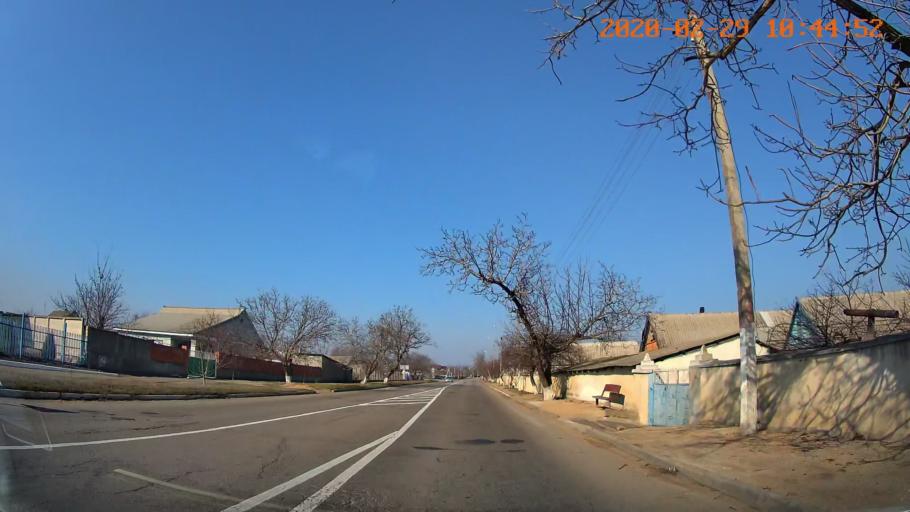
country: MD
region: Telenesti
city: Grigoriopol
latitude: 47.0725
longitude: 29.3895
